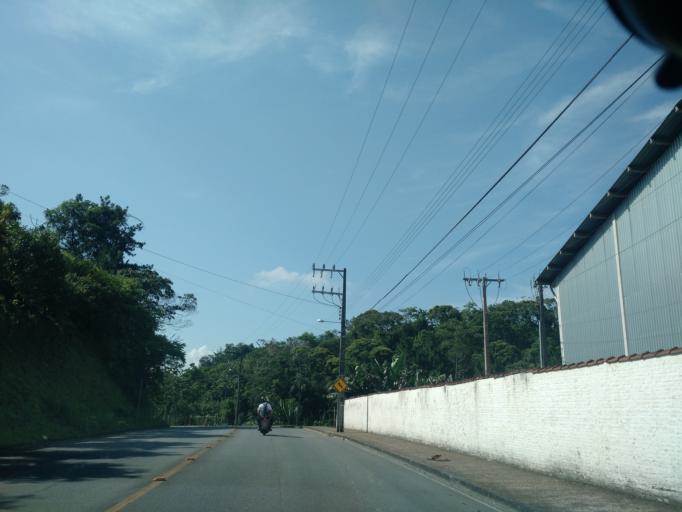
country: BR
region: Santa Catarina
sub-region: Jaragua Do Sul
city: Jaragua do Sul
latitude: -26.4969
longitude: -49.0993
